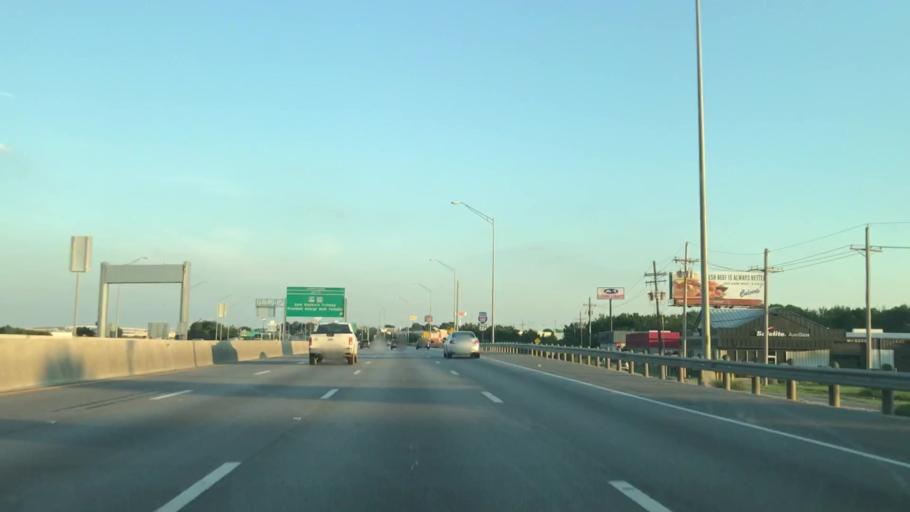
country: US
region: Texas
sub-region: Denton County
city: Lewisville
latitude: 33.0128
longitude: -96.9795
